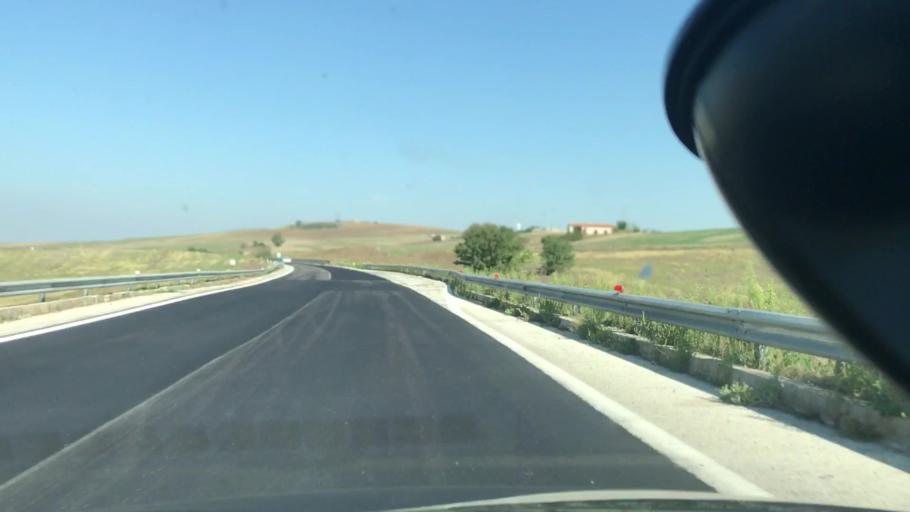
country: IT
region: Apulia
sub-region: Provincia di Barletta - Andria - Trani
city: Spinazzola
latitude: 40.9182
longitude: 16.1005
